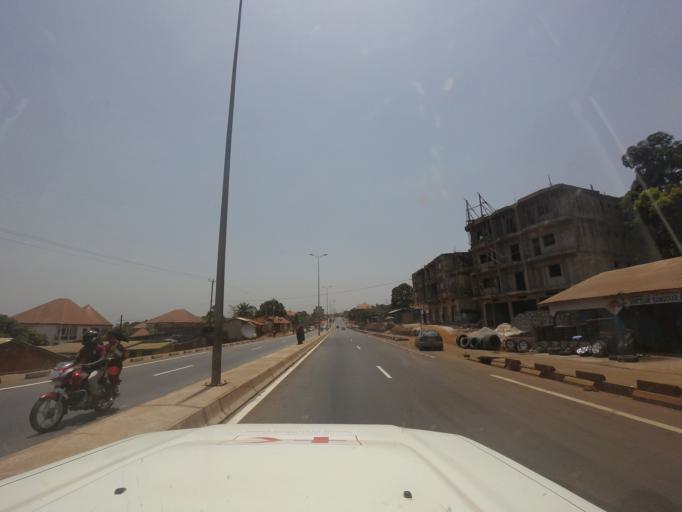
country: GN
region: Kindia
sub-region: Prefecture de Dubreka
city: Dubreka
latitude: 9.6941
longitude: -13.5061
